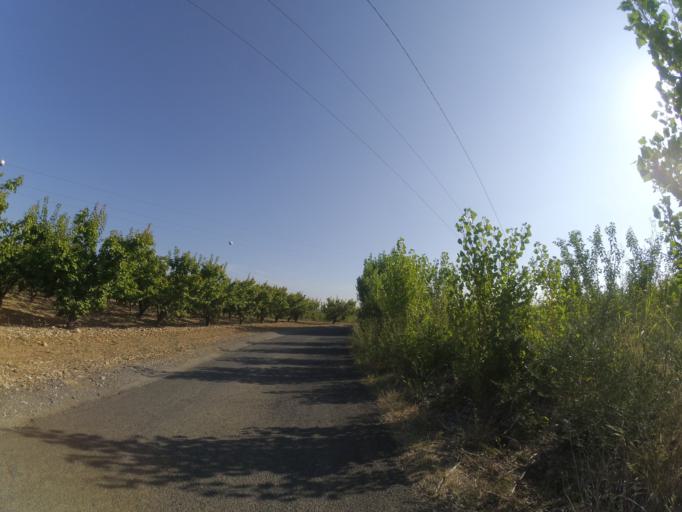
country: FR
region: Languedoc-Roussillon
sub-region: Departement des Pyrenees-Orientales
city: Peyrestortes
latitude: 42.7854
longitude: 2.8408
